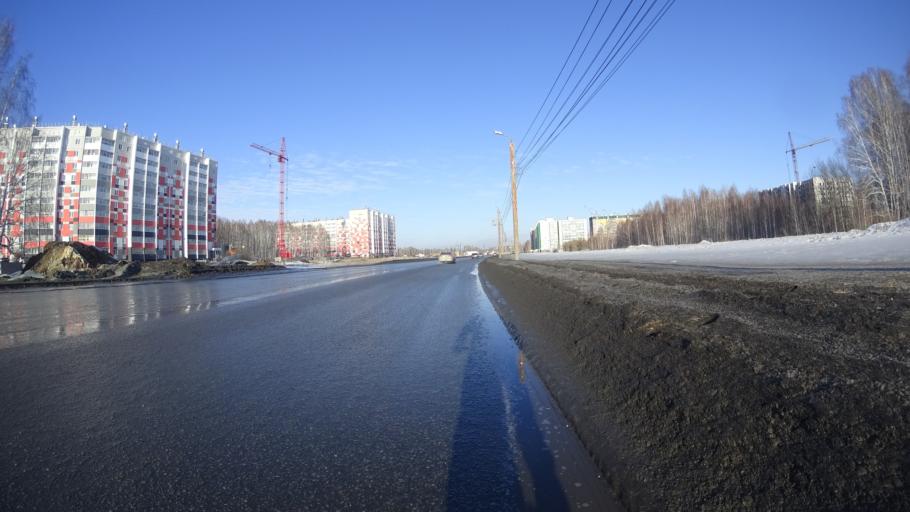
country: RU
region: Chelyabinsk
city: Roshchino
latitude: 55.2160
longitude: 61.2870
